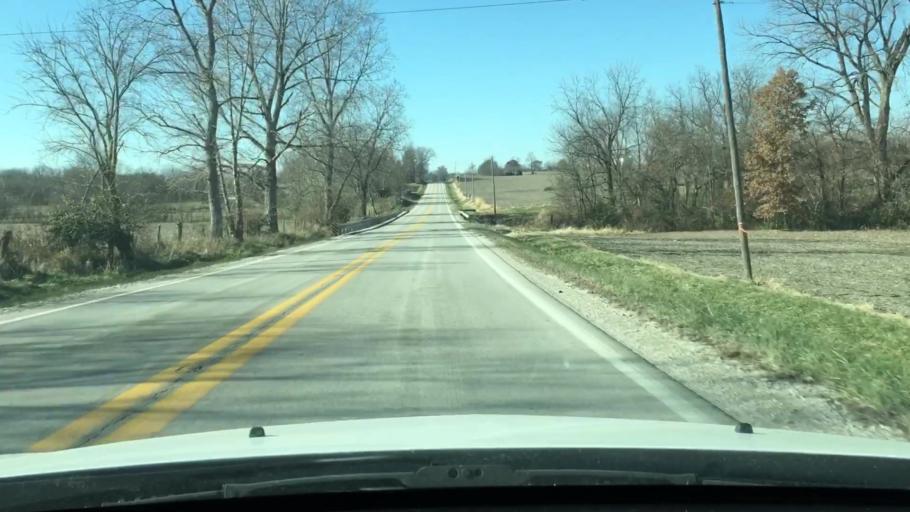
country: US
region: Illinois
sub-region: Pike County
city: Pittsfield
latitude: 39.6141
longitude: -90.7385
